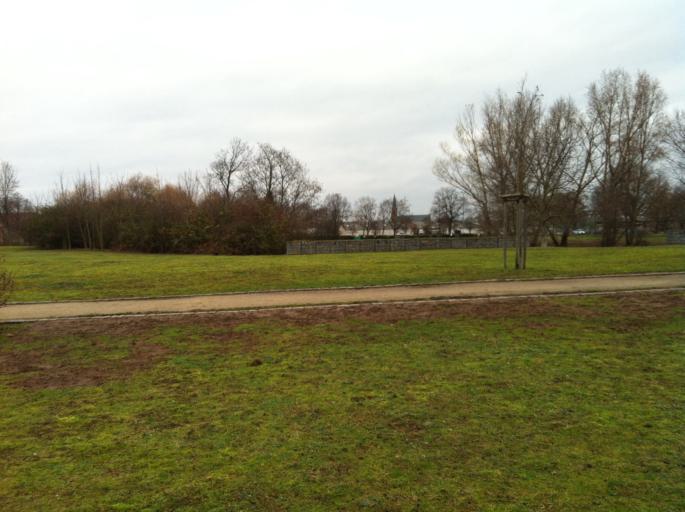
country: DE
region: Rheinland-Pfalz
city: Mainz
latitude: 49.9950
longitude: 8.3117
